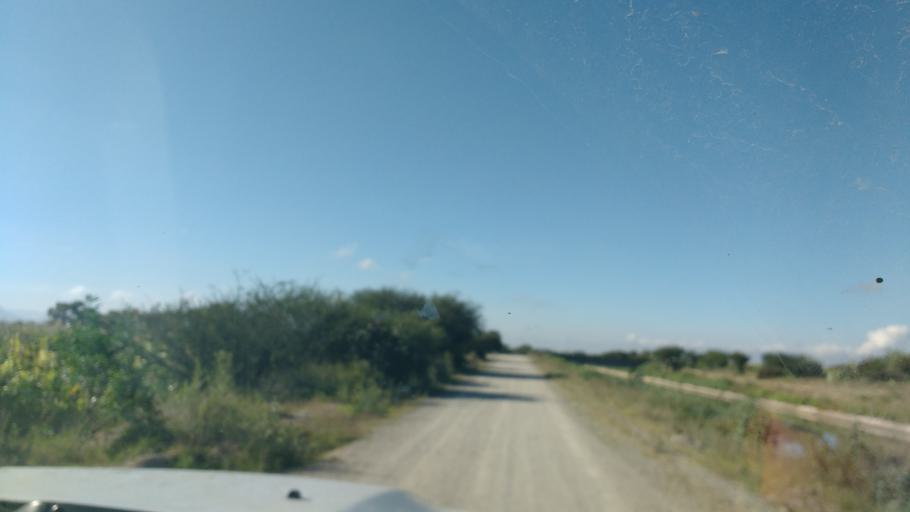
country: MX
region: Hidalgo
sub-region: Tezontepec de Aldama
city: Tenango
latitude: 20.2495
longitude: -99.2537
